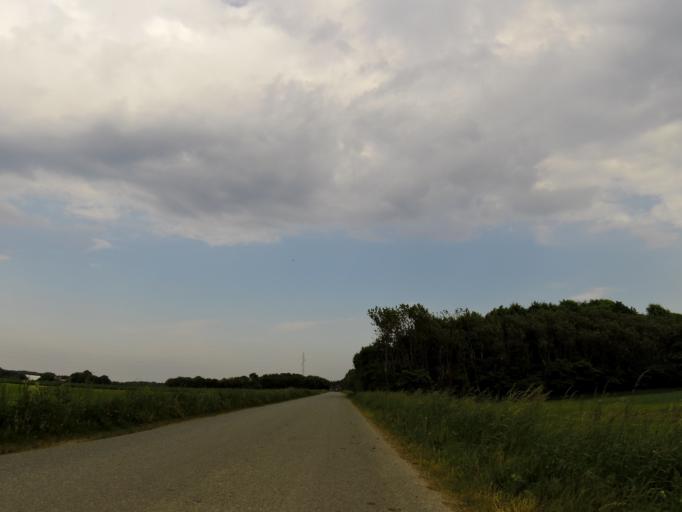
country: DK
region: Central Jutland
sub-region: Holstebro Kommune
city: Vinderup
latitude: 56.4982
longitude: 8.7804
